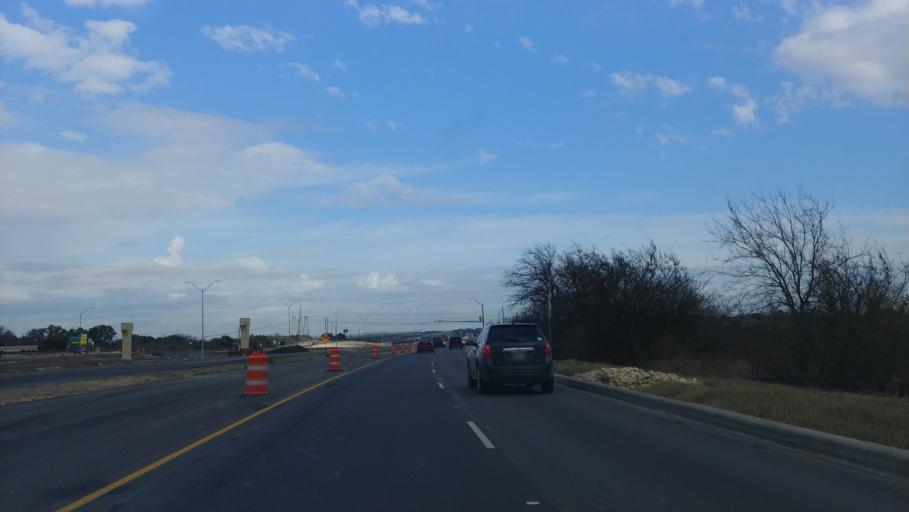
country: US
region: Texas
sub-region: Bexar County
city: Lackland Air Force Base
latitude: 29.4092
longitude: -98.7091
